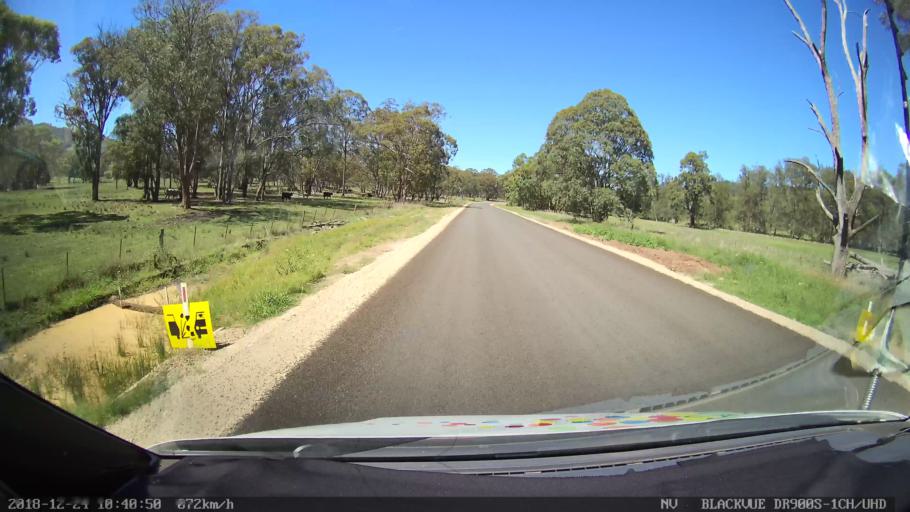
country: AU
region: New South Wales
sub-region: Upper Hunter Shire
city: Merriwa
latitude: -31.8646
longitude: 150.4641
